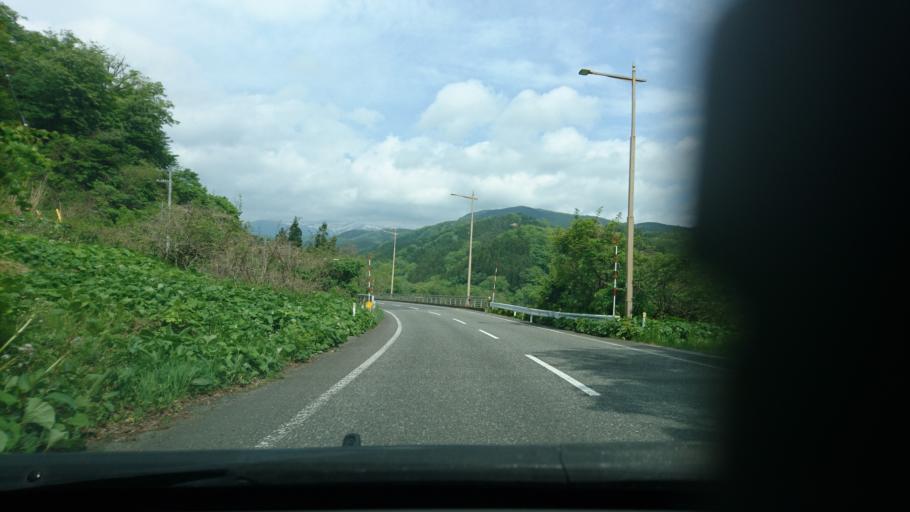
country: JP
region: Iwate
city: Ichinoseki
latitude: 38.9035
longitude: 140.9033
